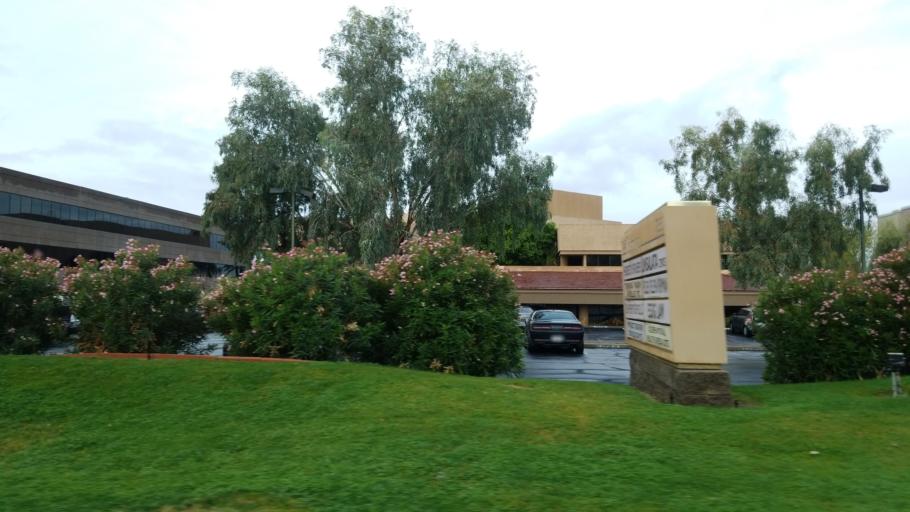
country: US
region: Arizona
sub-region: Maricopa County
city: Phoenix
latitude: 33.5448
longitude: -112.0477
